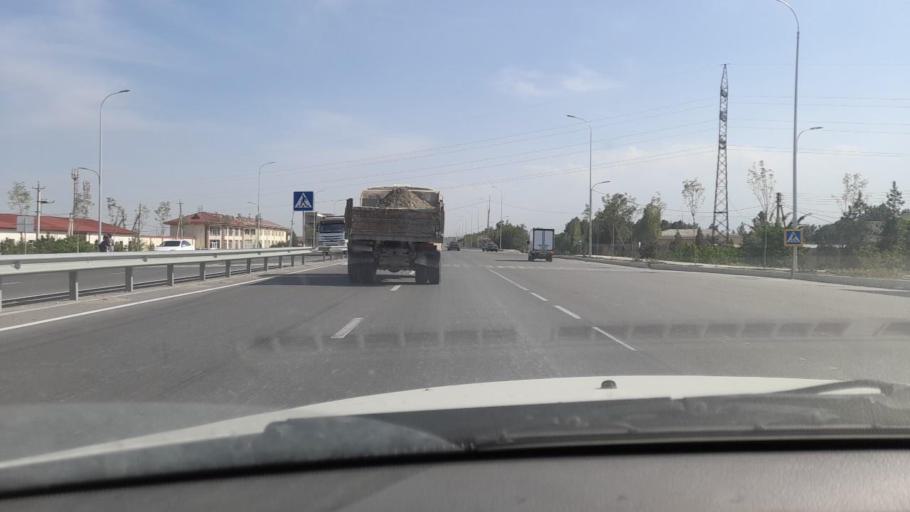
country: UZ
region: Samarqand
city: Daxbet
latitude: 39.7195
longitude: 66.9481
